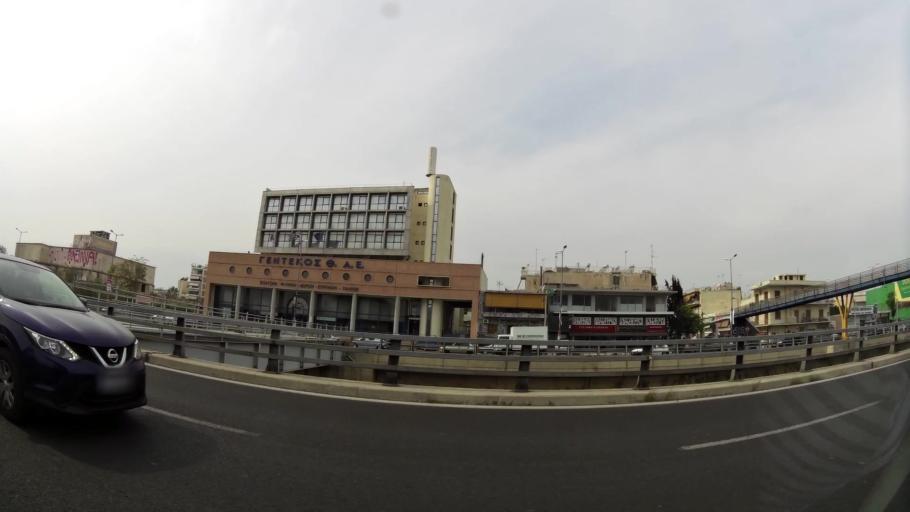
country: GR
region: Attica
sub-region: Nomos Piraios
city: Agios Ioannis Rentis
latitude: 37.9612
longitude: 23.6768
